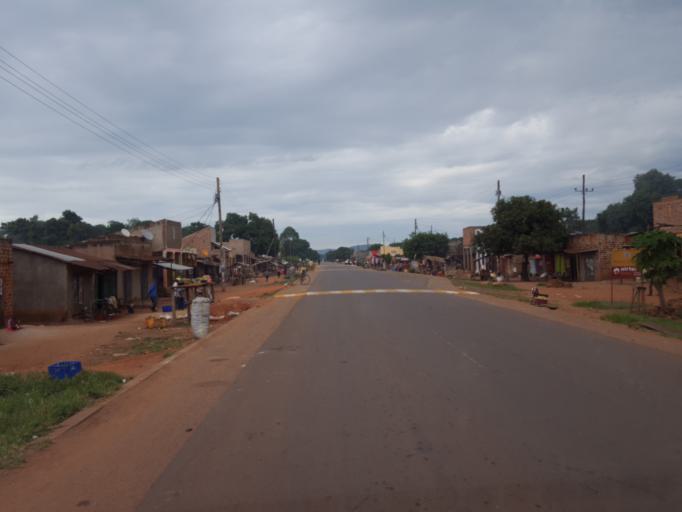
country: UG
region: Central Region
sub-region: Kiboga District
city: Kiboga
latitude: 1.0305
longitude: 31.6787
